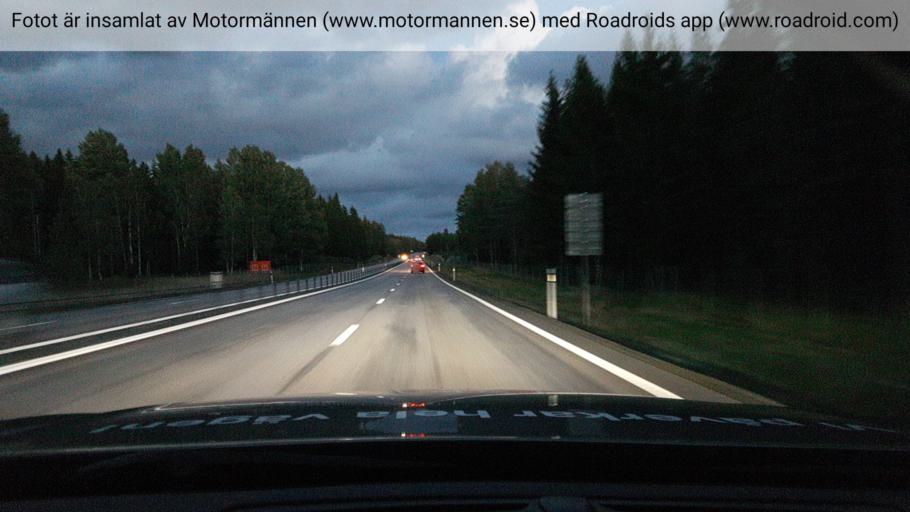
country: SE
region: Vaermland
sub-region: Kristinehamns Kommun
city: Kristinehamn
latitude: 59.3594
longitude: 14.0404
